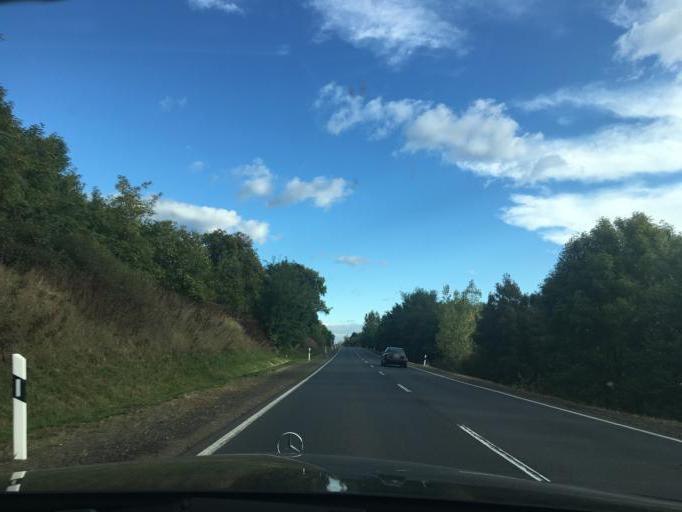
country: HU
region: Borsod-Abauj-Zemplen
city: Encs
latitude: 48.3770
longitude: 21.1466
